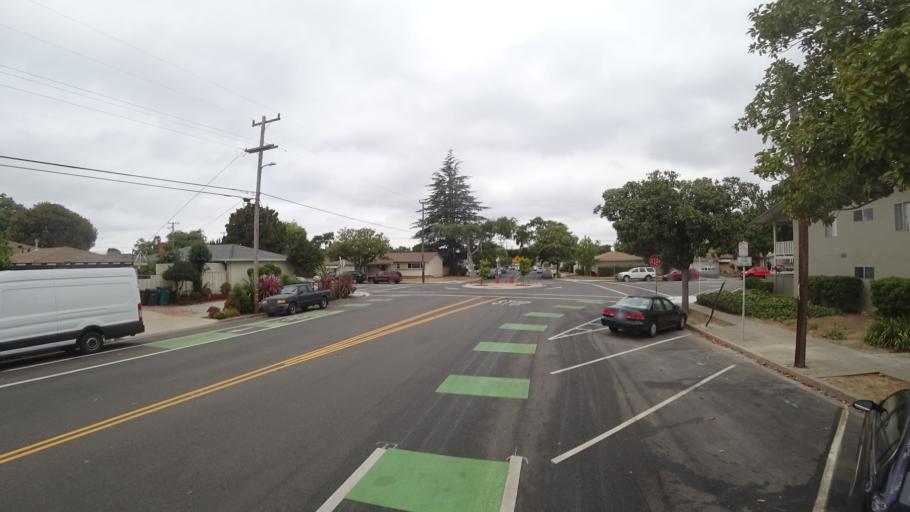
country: US
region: California
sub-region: Alameda County
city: Union City
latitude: 37.6187
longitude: -122.0389
